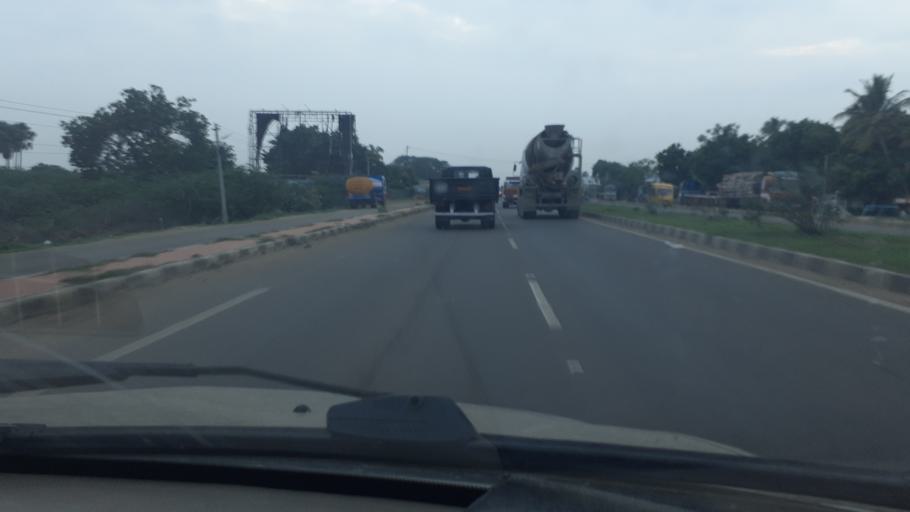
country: IN
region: Tamil Nadu
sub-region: Thoothukkudi
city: Korampallam
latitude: 8.7811
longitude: 78.0986
